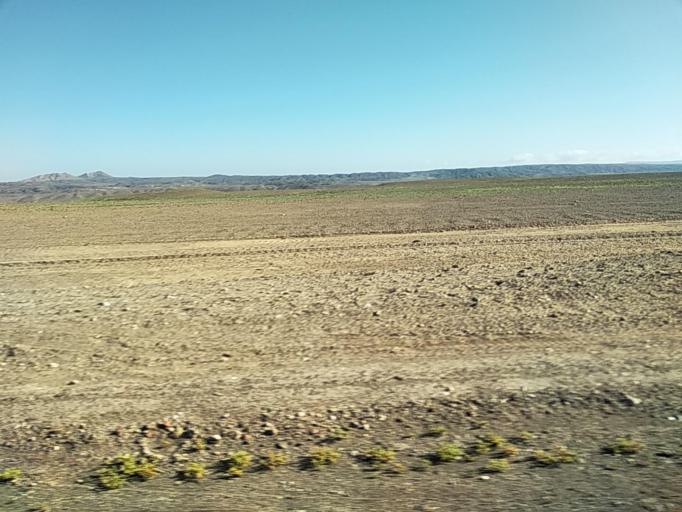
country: CL
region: Atacama
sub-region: Provincia de Copiapo
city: Copiapo
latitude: -27.3293
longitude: -70.7700
